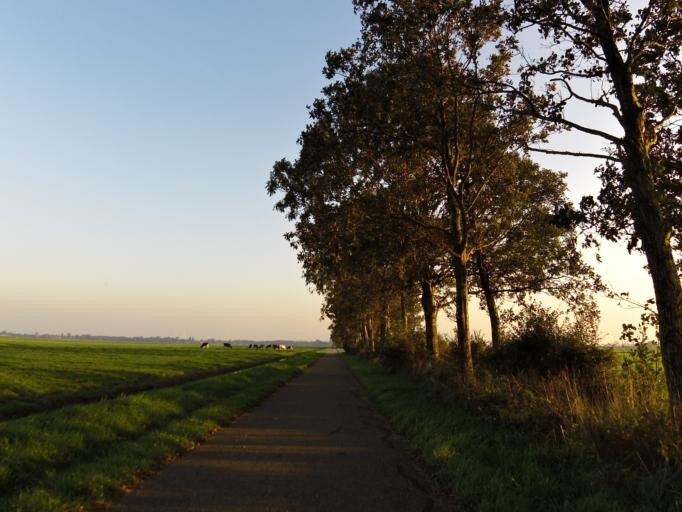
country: NL
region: South Holland
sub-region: Gemeente Leiderdorp
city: Leiderdorp
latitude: 52.1510
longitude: 4.5826
